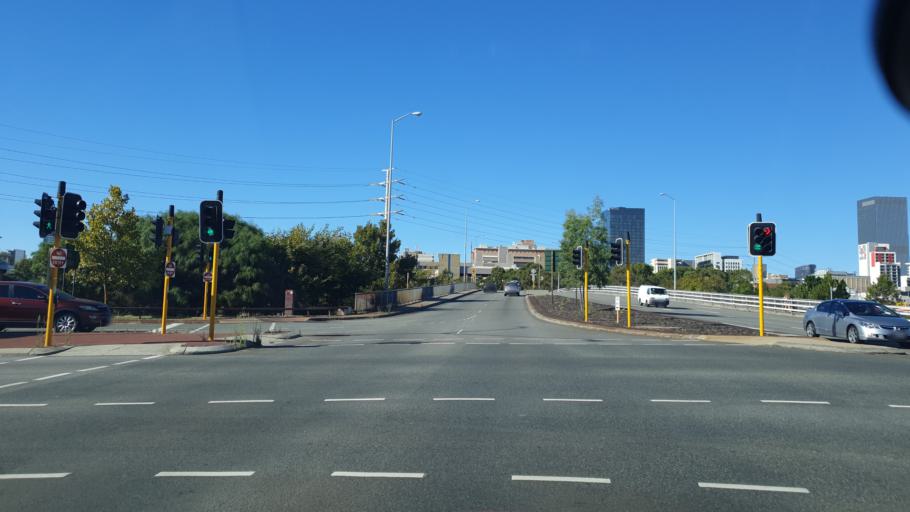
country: AU
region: Western Australia
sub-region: Cambridge
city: Perth
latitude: -31.9497
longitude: 115.8691
